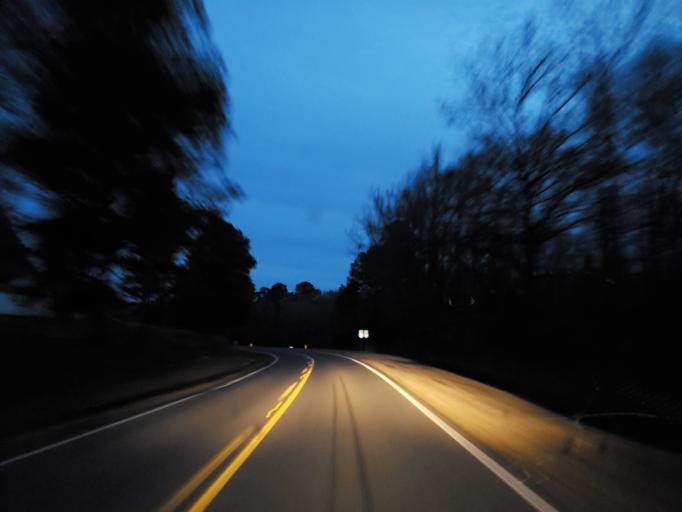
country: US
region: Alabama
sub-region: Greene County
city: Eutaw
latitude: 32.8718
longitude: -87.9280
